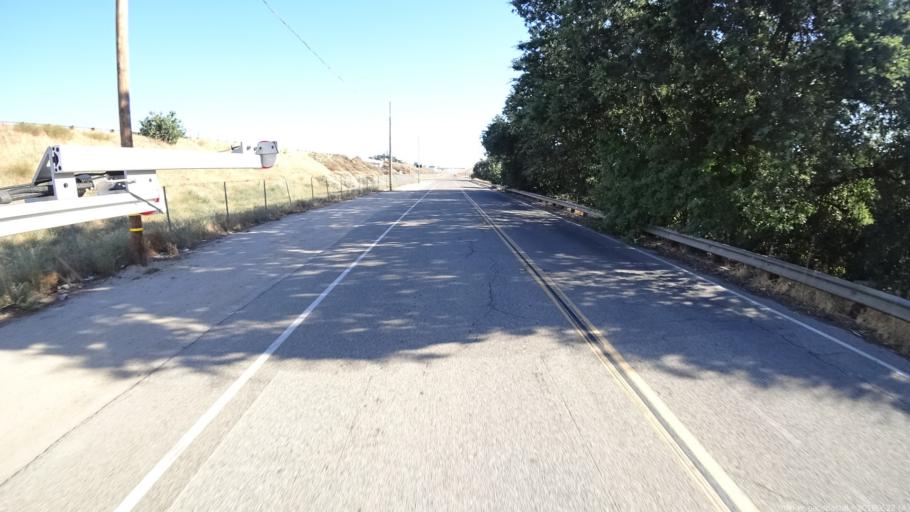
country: US
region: California
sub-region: Fresno County
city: Clovis
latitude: 36.8797
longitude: -119.7923
